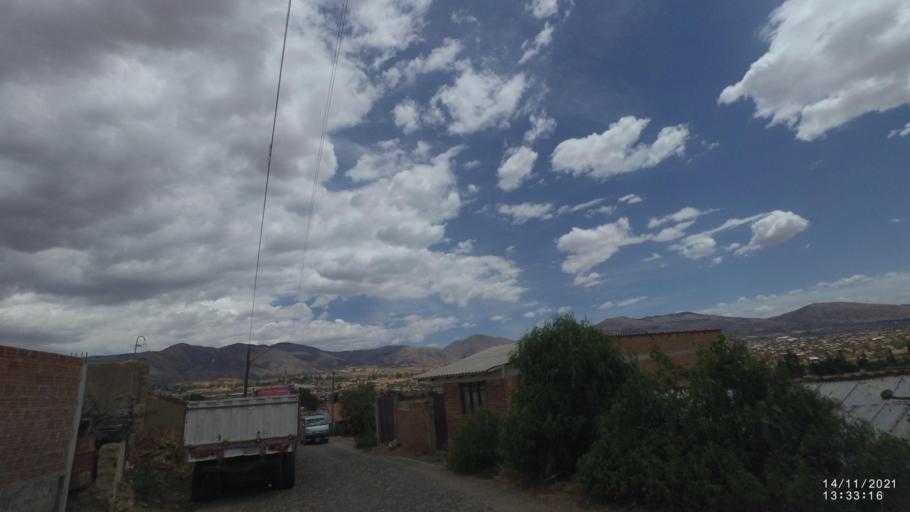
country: BO
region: Cochabamba
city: Colomi
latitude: -17.3989
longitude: -65.9853
